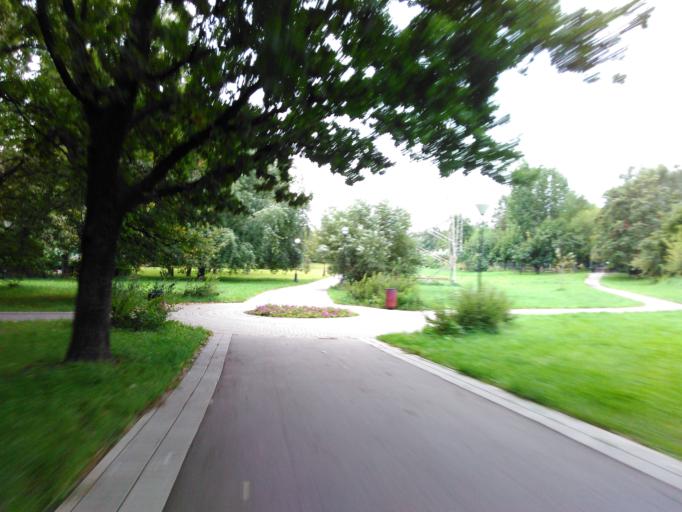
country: RU
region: Moscow
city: Zyuzino
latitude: 55.6480
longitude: 37.5856
